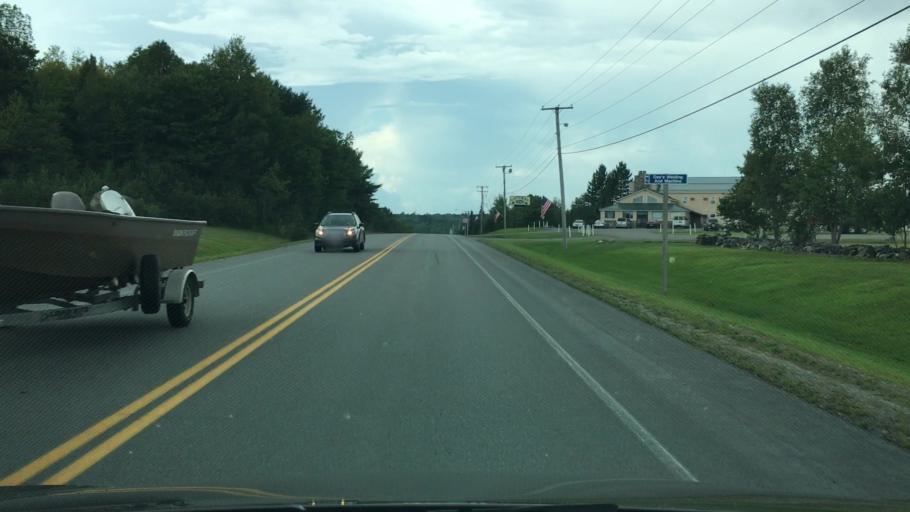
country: US
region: Maine
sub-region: Penobscot County
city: Medway
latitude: 45.6113
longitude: -68.5270
